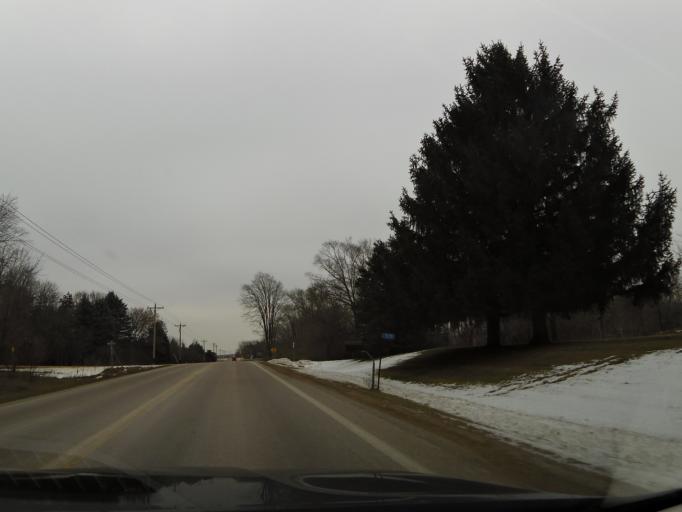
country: US
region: Minnesota
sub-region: Carver County
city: Carver
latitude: 44.7181
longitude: -93.6526
